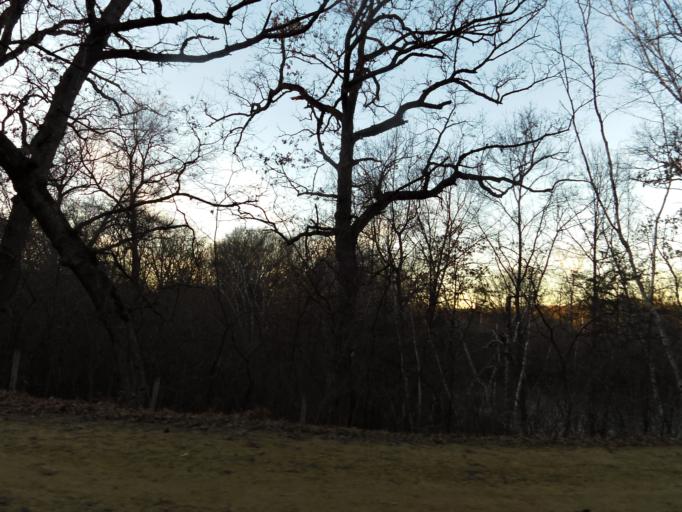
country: US
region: Minnesota
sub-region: Washington County
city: Grant
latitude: 45.0756
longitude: -92.9024
